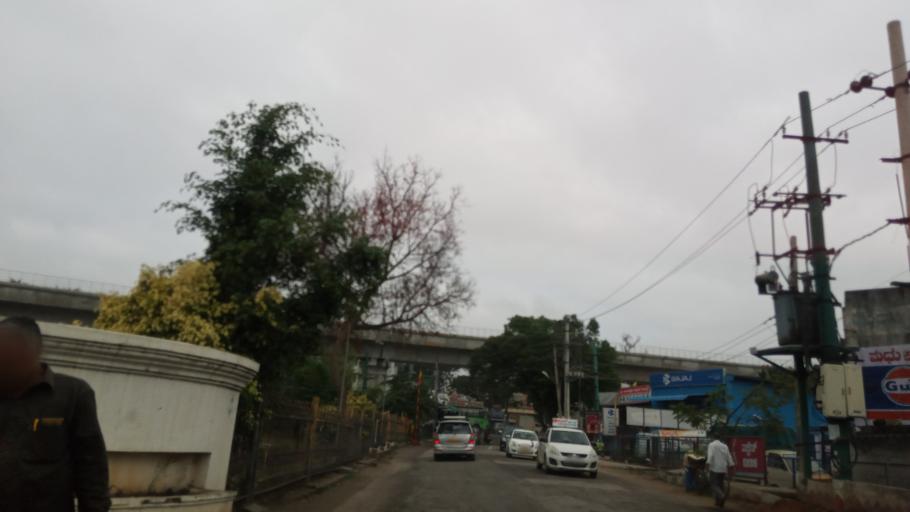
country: IN
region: Karnataka
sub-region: Bangalore Urban
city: Bangalore
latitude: 12.9120
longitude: 77.4857
